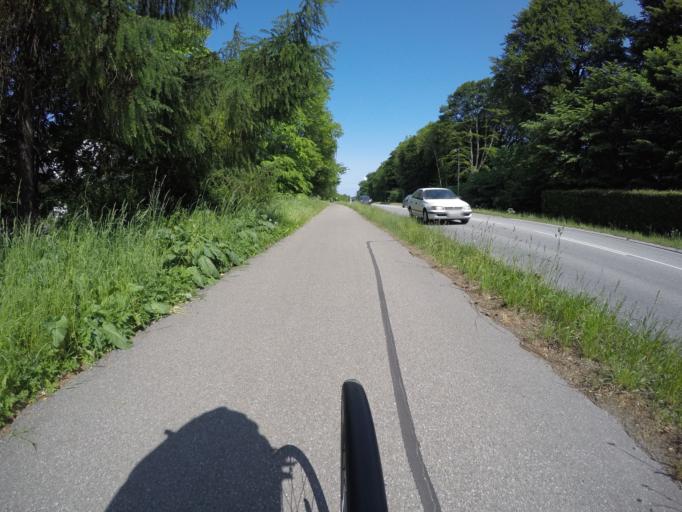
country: DK
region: Capital Region
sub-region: Horsholm Kommune
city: Horsholm
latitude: 55.8718
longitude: 12.4978
